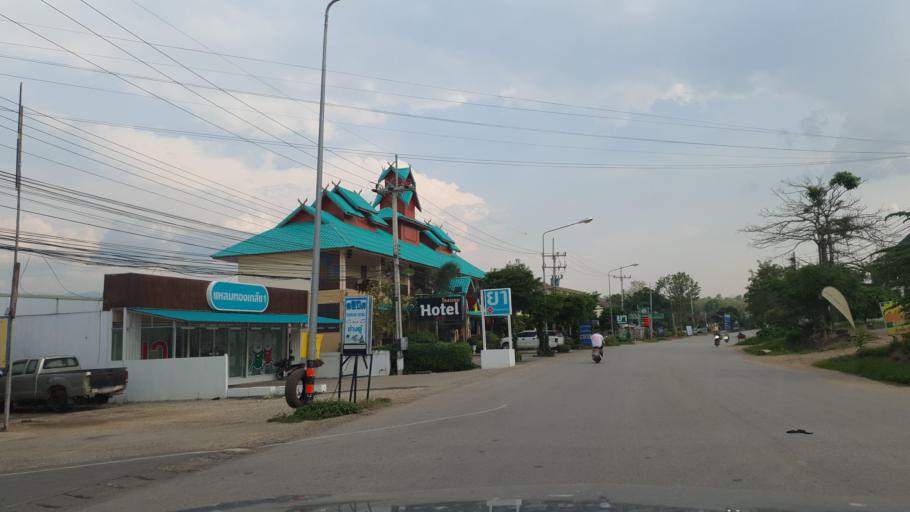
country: TH
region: Chiang Mai
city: Pai
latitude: 19.3509
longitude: 98.4354
